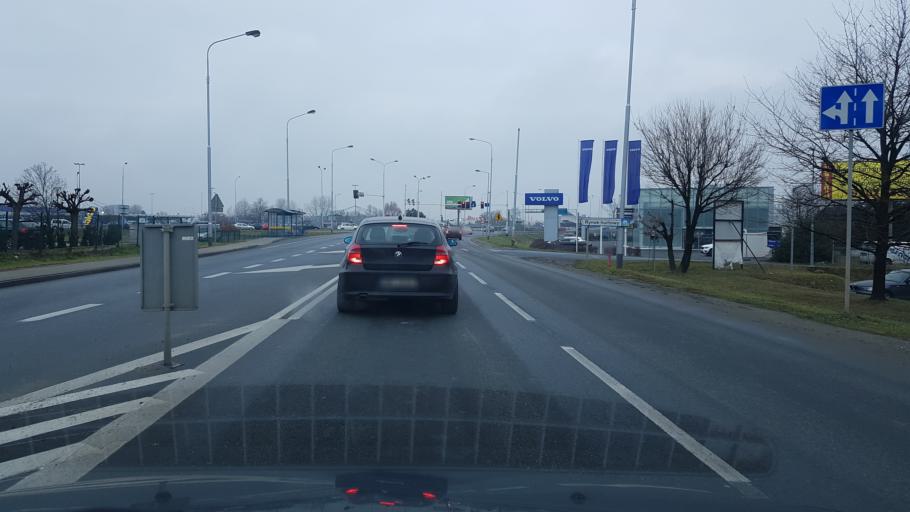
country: PL
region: Lower Silesian Voivodeship
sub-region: Powiat wroclawski
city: Bielany Wroclawskie
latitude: 51.0459
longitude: 16.9706
